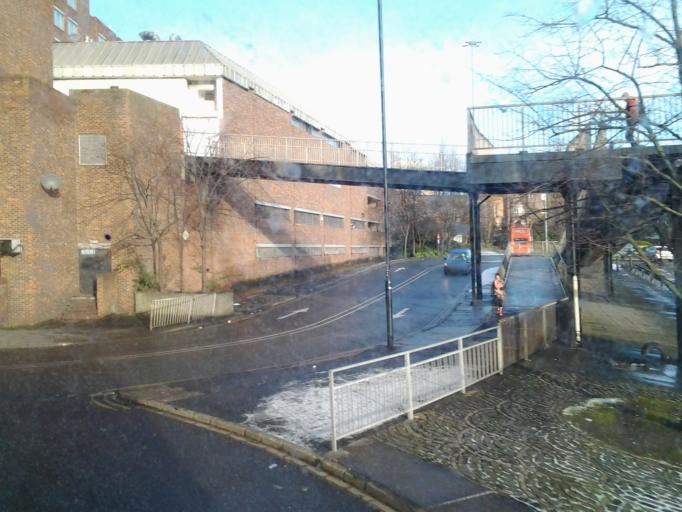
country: GB
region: England
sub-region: Newcastle upon Tyne
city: Newcastle upon Tyne
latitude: 54.9742
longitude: -1.6072
